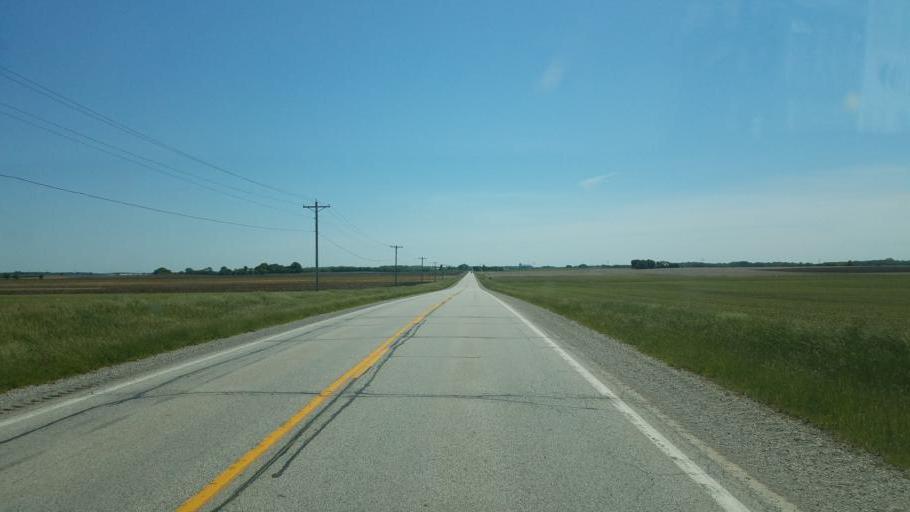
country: US
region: Illinois
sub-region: McLean County
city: Heyworth
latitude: 40.3120
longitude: -89.0547
